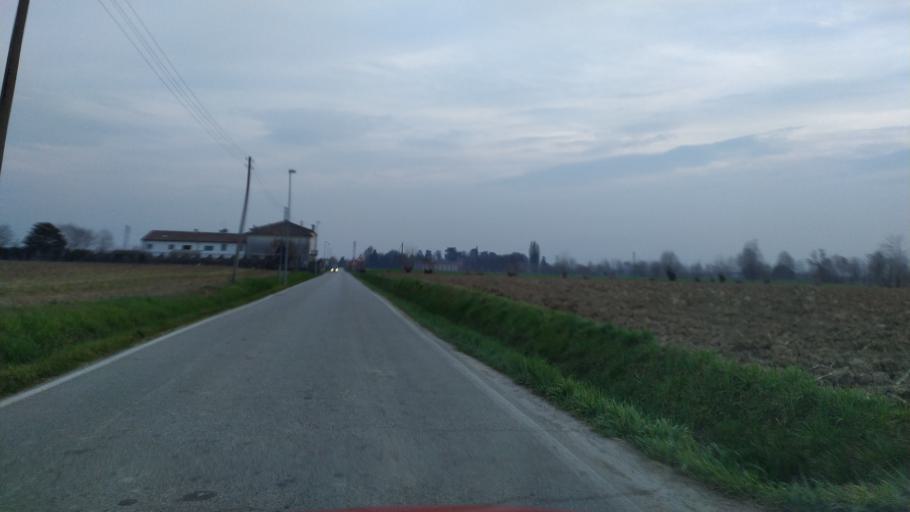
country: IT
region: Veneto
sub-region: Provincia di Vicenza
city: Vigardolo
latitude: 45.6187
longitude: 11.5858
